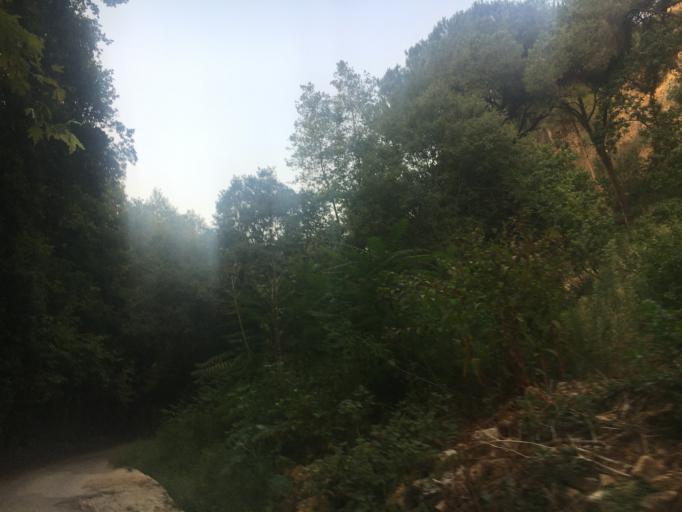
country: LB
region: Mont-Liban
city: Djounie
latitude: 33.9670
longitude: 35.6440
